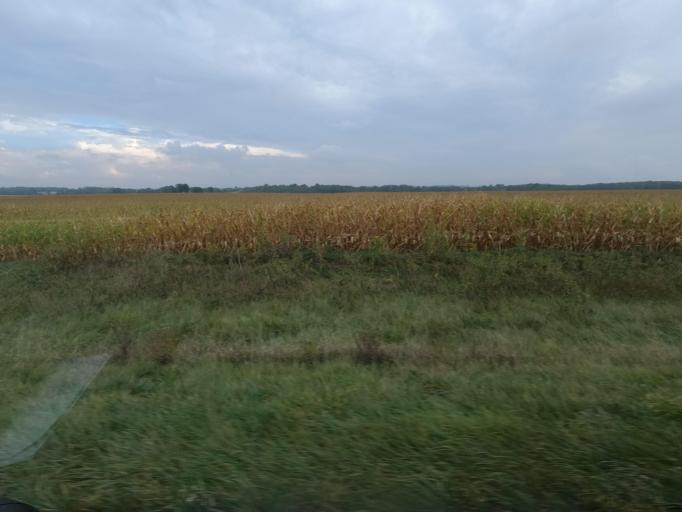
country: US
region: Iowa
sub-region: Van Buren County
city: Keosauqua
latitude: 40.8133
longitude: -91.7800
